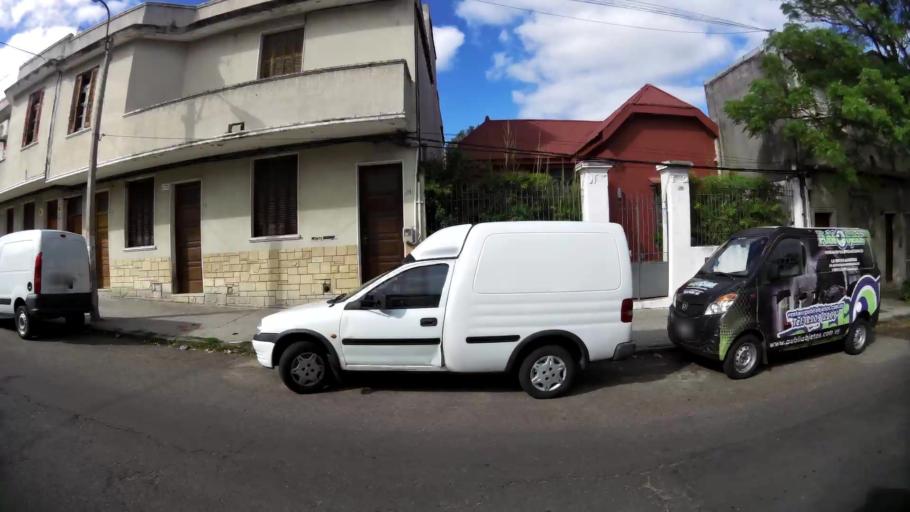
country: UY
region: Montevideo
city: Montevideo
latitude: -34.8813
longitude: -56.1572
